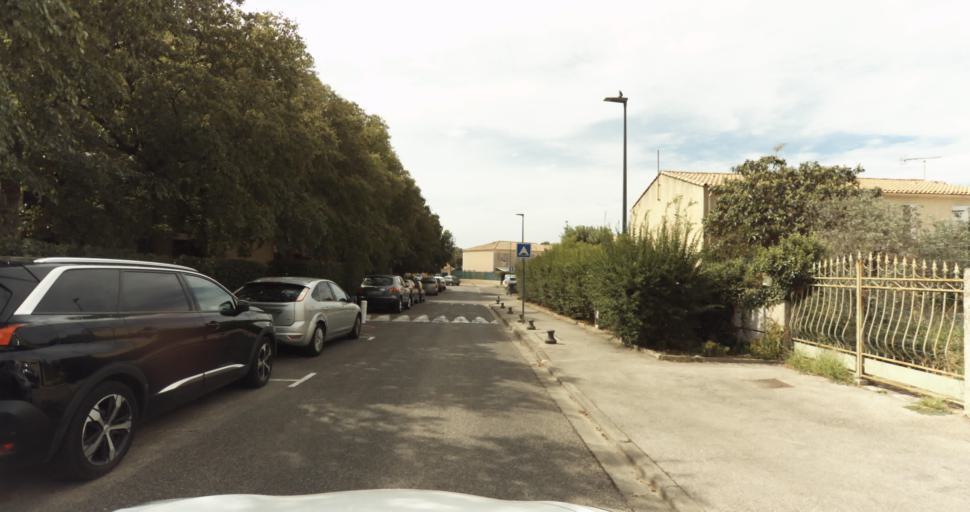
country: FR
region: Provence-Alpes-Cote d'Azur
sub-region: Departement des Bouches-du-Rhone
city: Miramas
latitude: 43.5749
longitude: 4.9968
